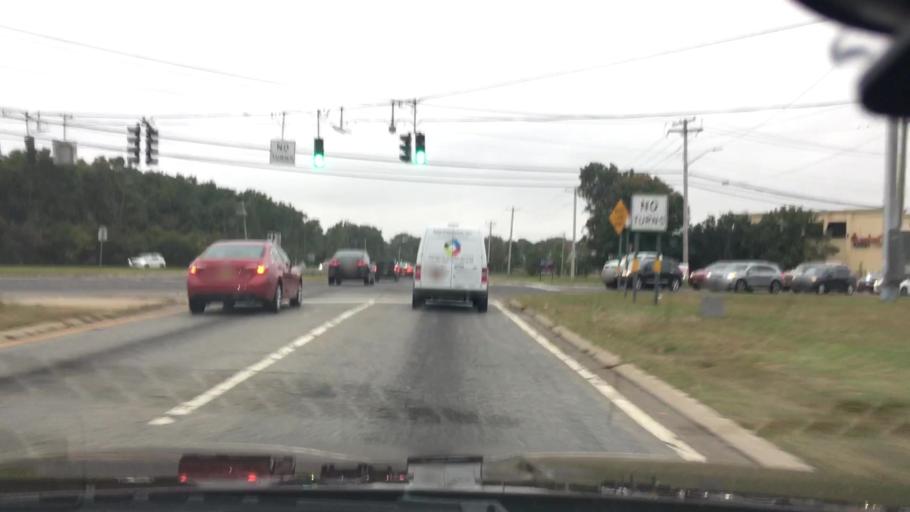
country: US
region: New York
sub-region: Suffolk County
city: Nesconset
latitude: 40.8620
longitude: -73.1389
